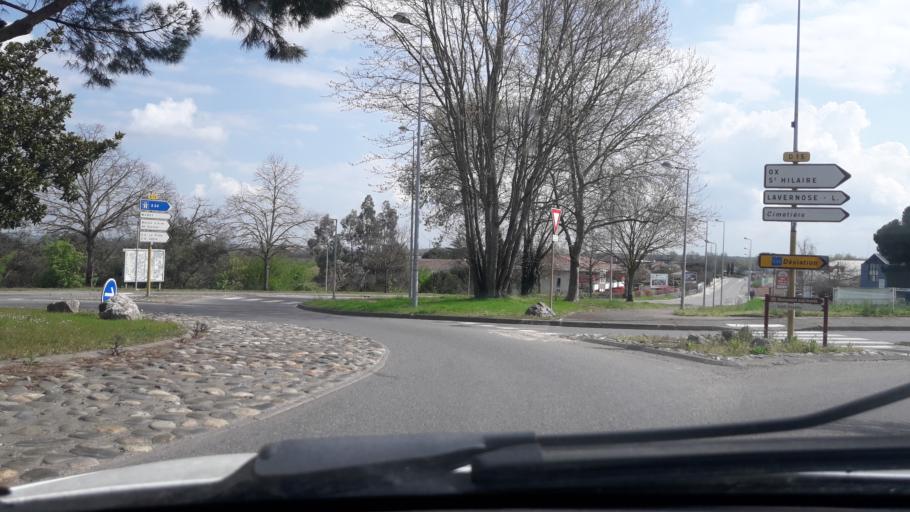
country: FR
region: Midi-Pyrenees
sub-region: Departement de la Haute-Garonne
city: Seysses
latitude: 43.4936
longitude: 1.3127
